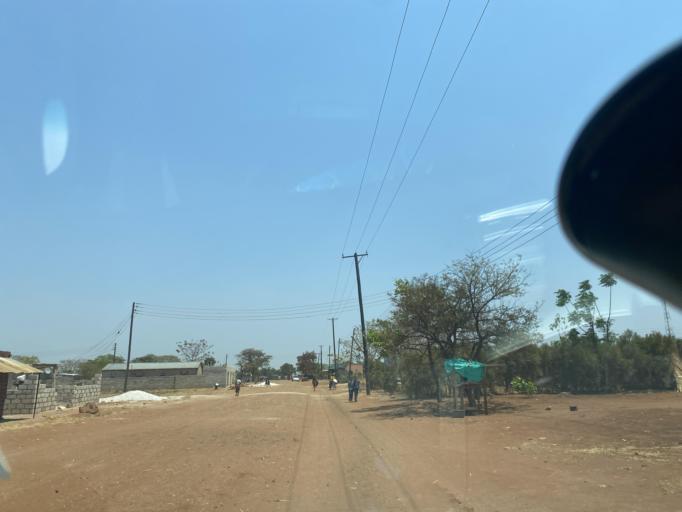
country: ZM
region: Southern
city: Nakambala
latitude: -15.5126
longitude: 27.9299
